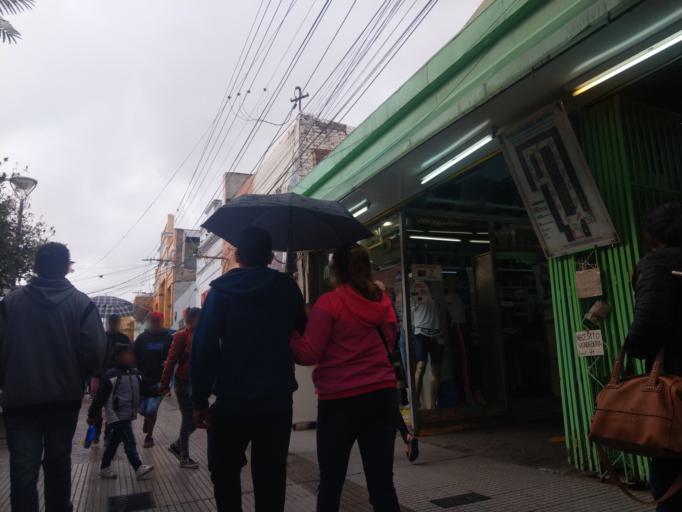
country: AR
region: Salta
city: Salta
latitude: -24.7926
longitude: -65.4127
